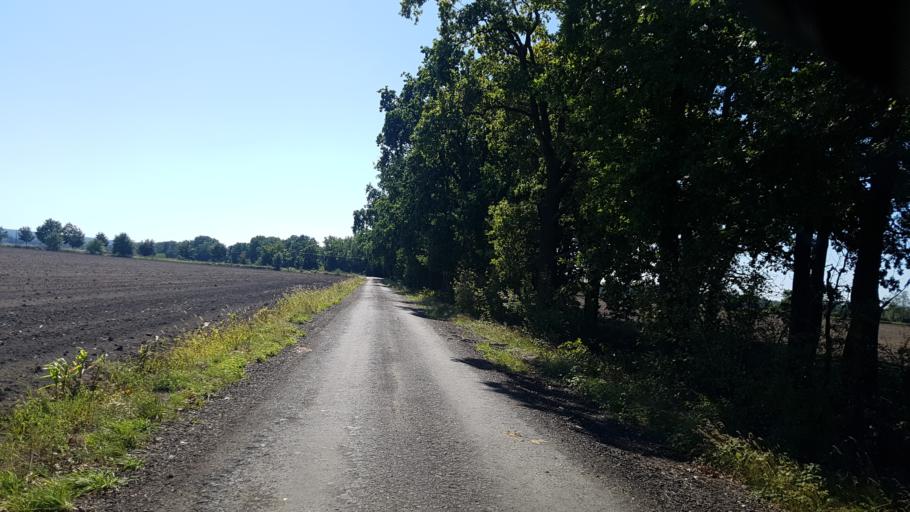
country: DE
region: Brandenburg
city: Elsterwerda
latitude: 51.4476
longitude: 13.5409
